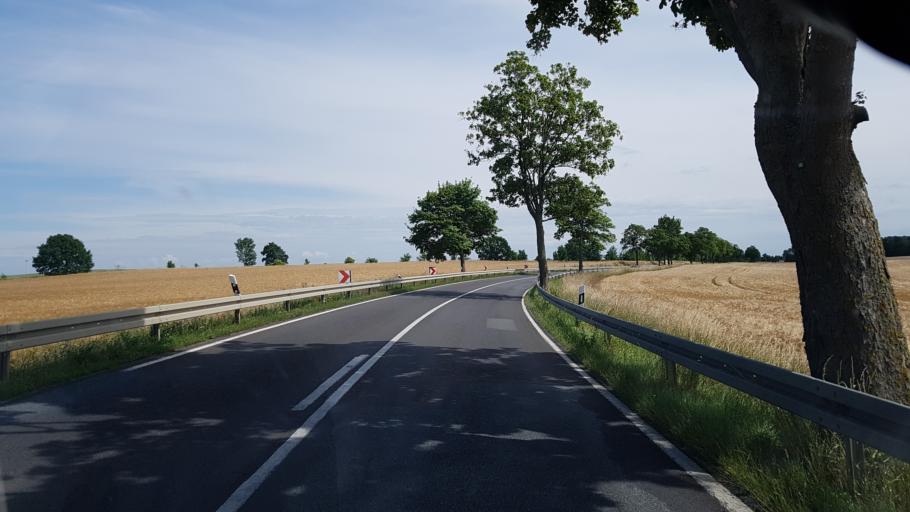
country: DE
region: Mecklenburg-Vorpommern
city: Strasburg
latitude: 53.3939
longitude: 13.7688
